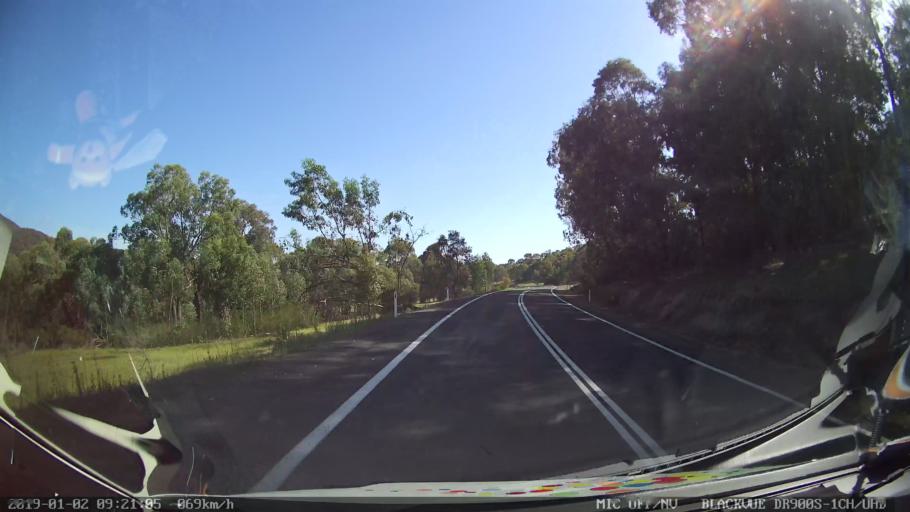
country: AU
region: New South Wales
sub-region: Tumut Shire
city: Tumut
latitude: -35.4095
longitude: 148.2898
